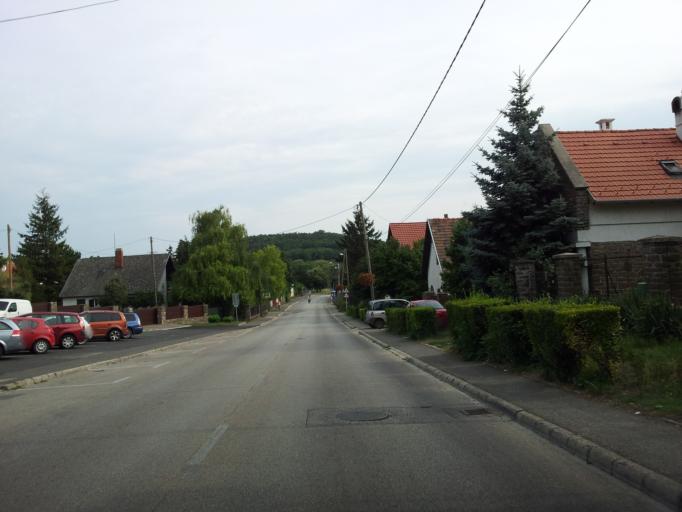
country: HU
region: Veszprem
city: Tihany
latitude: 46.9101
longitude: 17.8901
